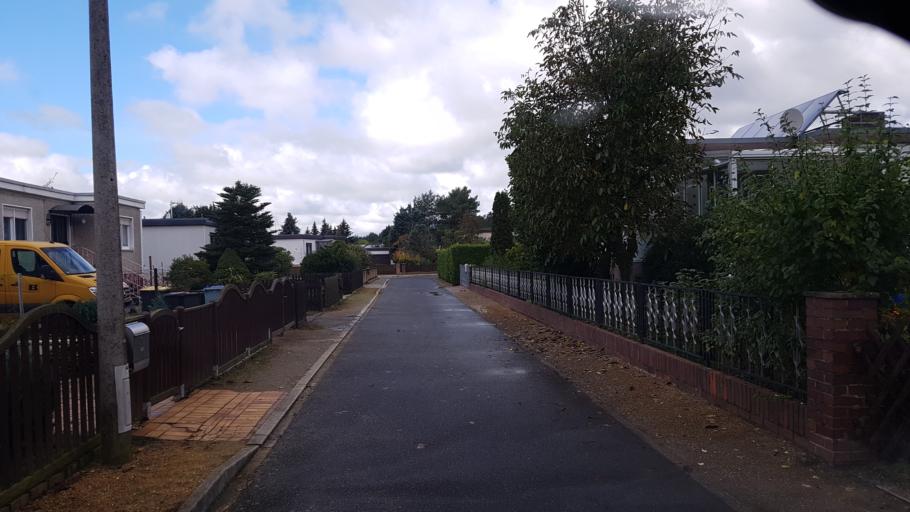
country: DE
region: Brandenburg
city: Grossraschen
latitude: 51.6033
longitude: 14.0091
